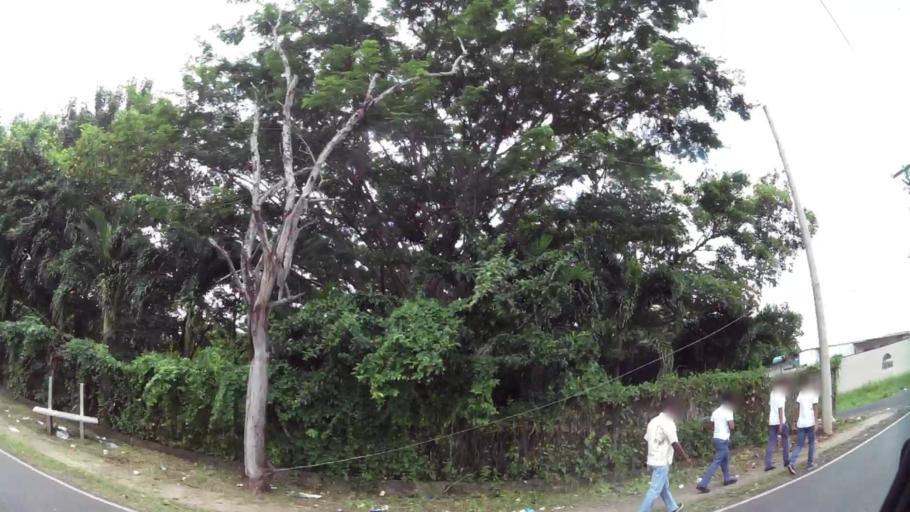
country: PA
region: Panama
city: San Miguelito
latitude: 9.0473
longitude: -79.4354
